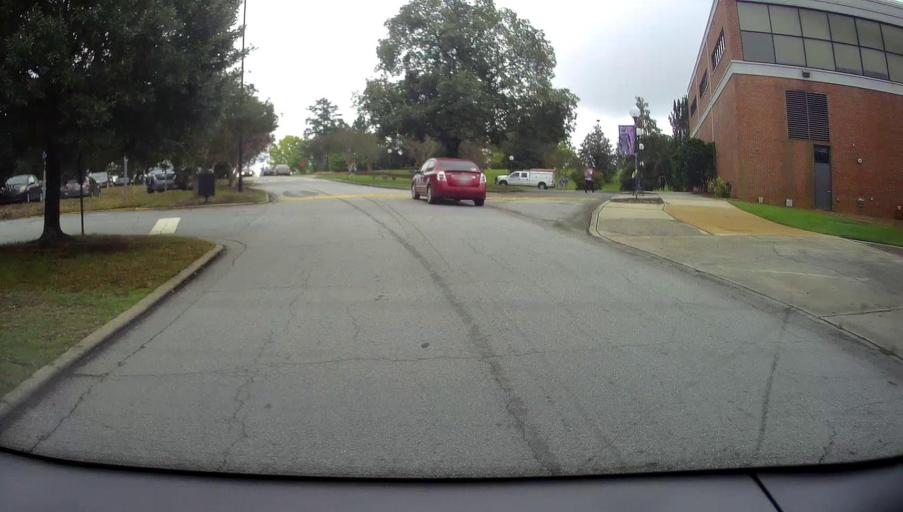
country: US
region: Georgia
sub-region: Bibb County
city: West Point
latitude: 32.8099
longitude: -83.7319
